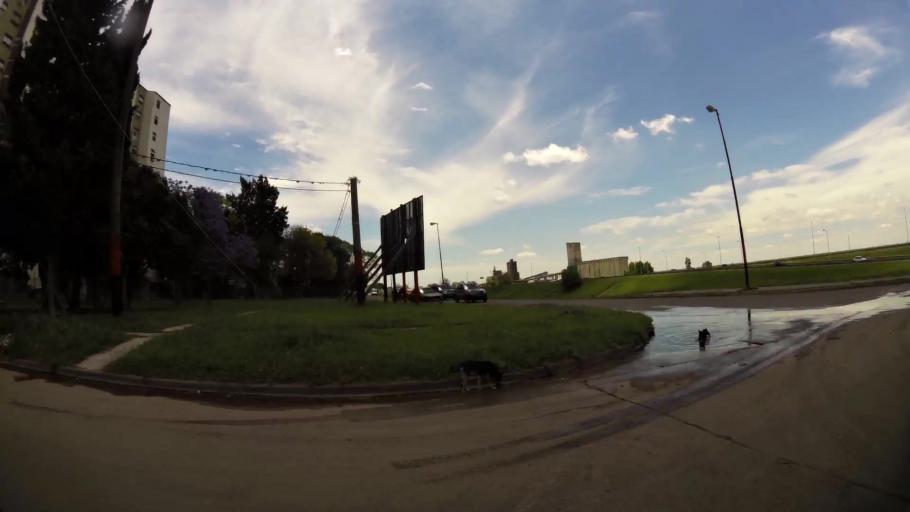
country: AR
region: Santa Fe
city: Gobernador Galvez
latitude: -32.9932
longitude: -60.6215
